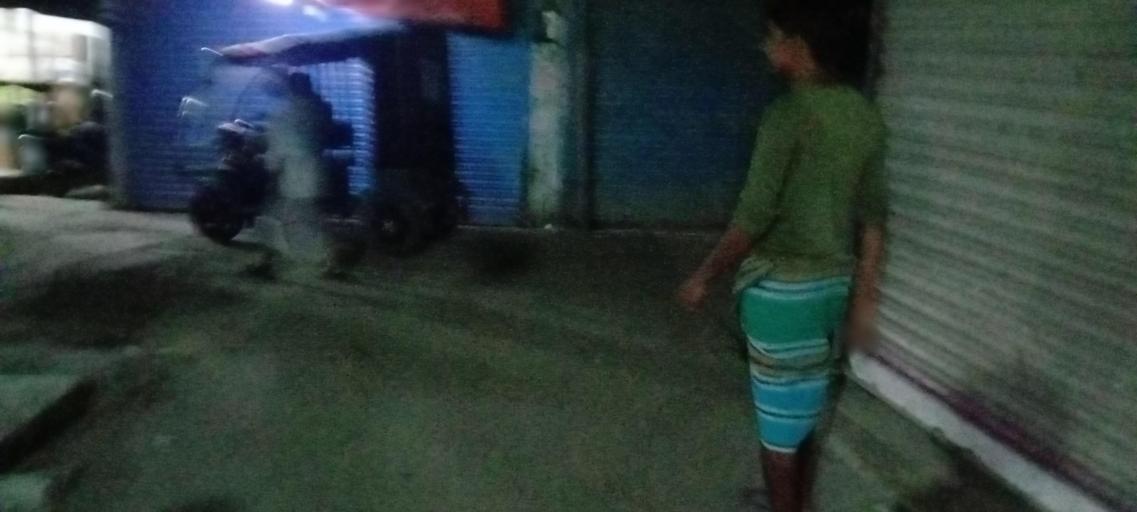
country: BD
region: Dhaka
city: Azimpur
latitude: 23.6862
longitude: 90.3075
